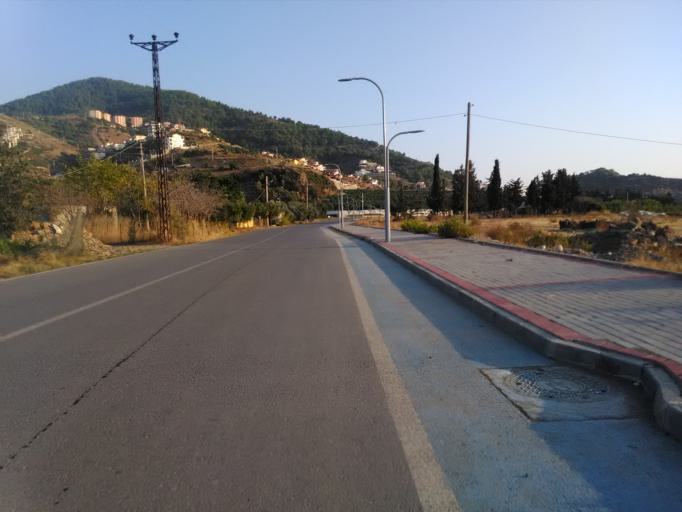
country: TR
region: Antalya
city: Gazipasa
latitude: 36.2426
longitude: 32.2982
